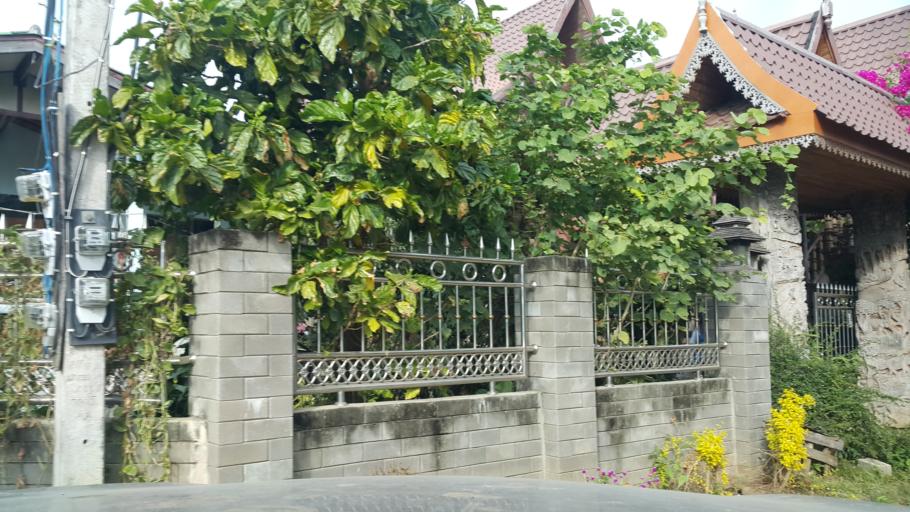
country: TH
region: Sukhothai
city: Thung Saliam
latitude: 17.3170
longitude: 99.5643
